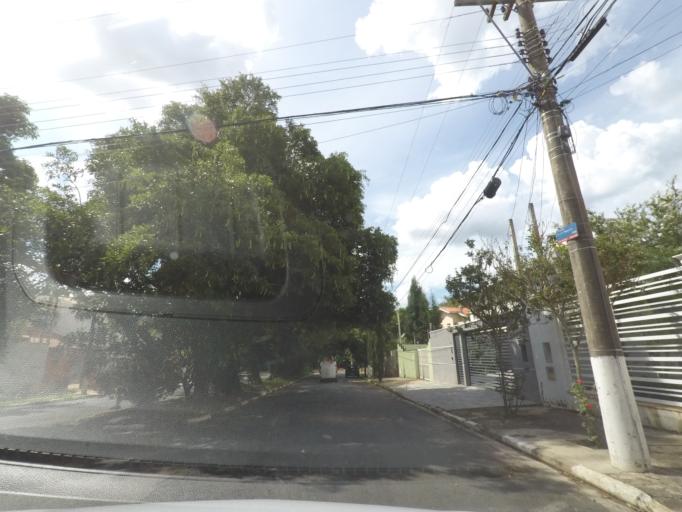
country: BR
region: Sao Paulo
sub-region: Campinas
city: Campinas
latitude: -22.8889
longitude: -47.0942
